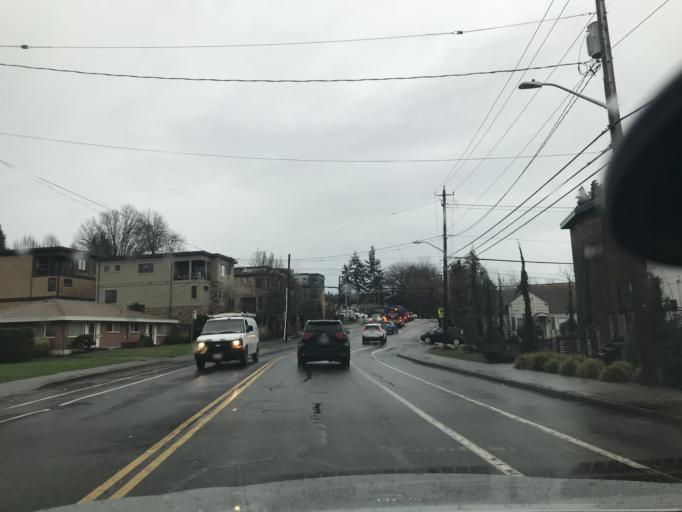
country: US
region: Washington
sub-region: King County
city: Kirkland
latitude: 47.6681
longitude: -122.2021
